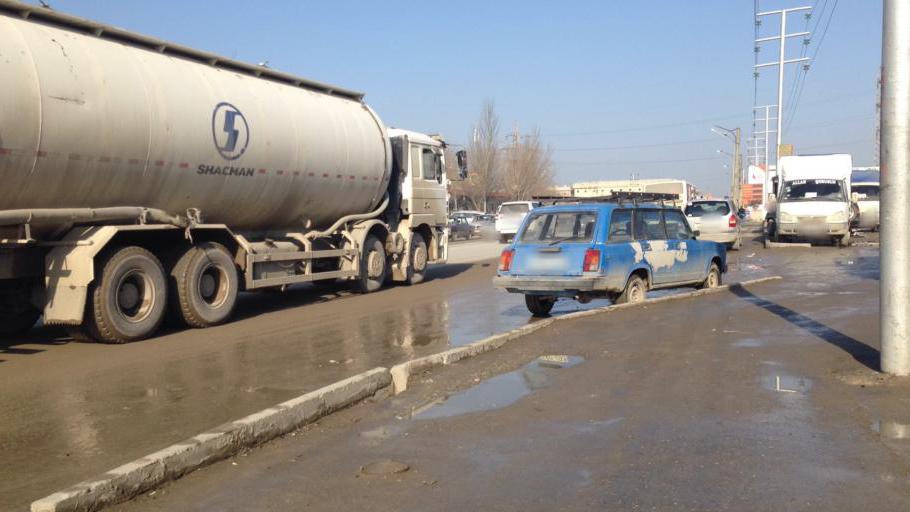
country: AZ
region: Baki
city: Binagadi
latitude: 40.4408
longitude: 49.8450
